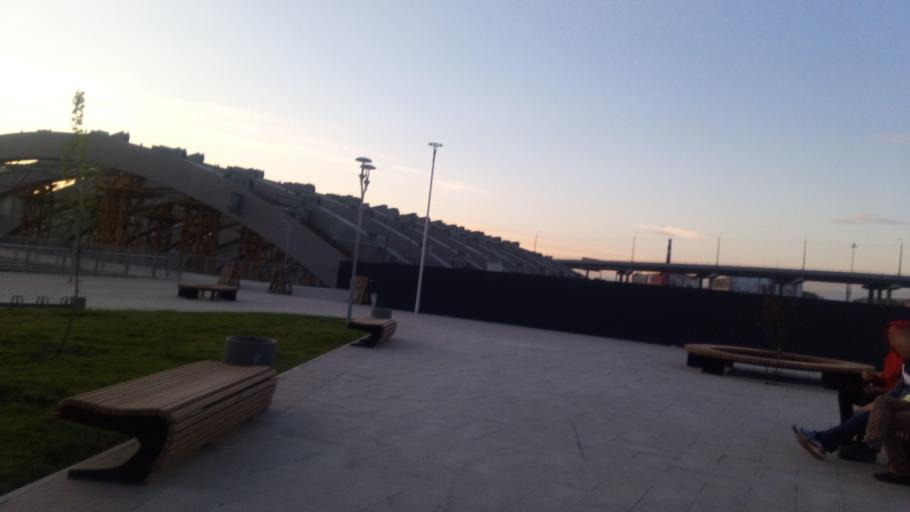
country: RU
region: Chelyabinsk
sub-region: Gorod Chelyabinsk
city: Chelyabinsk
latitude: 55.1698
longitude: 61.4086
